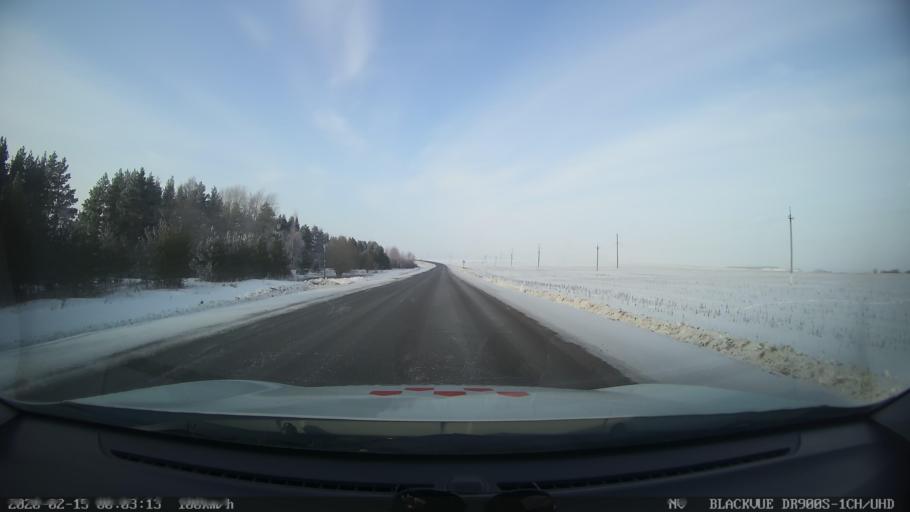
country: RU
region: Tatarstan
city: Kuybyshevskiy Zaton
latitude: 55.3689
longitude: 48.9991
